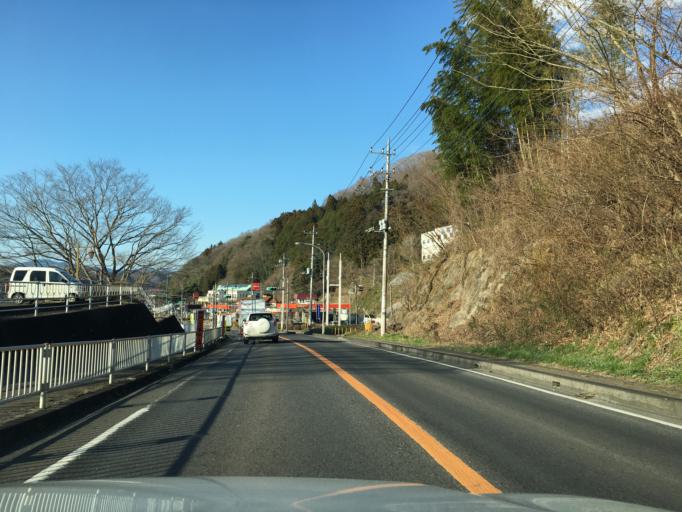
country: JP
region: Ibaraki
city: Daigo
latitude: 36.7656
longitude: 140.3591
